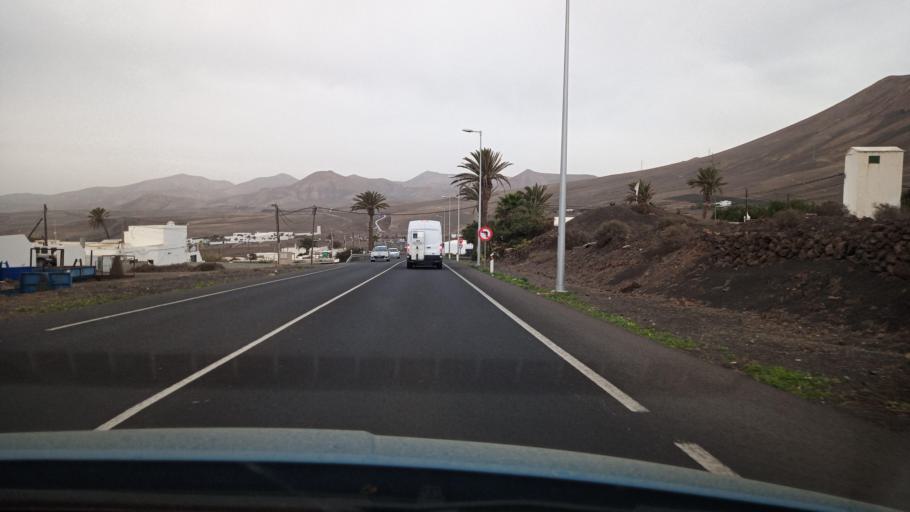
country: ES
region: Canary Islands
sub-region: Provincia de Las Palmas
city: Puerto del Carmen
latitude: 28.9455
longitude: -13.6981
